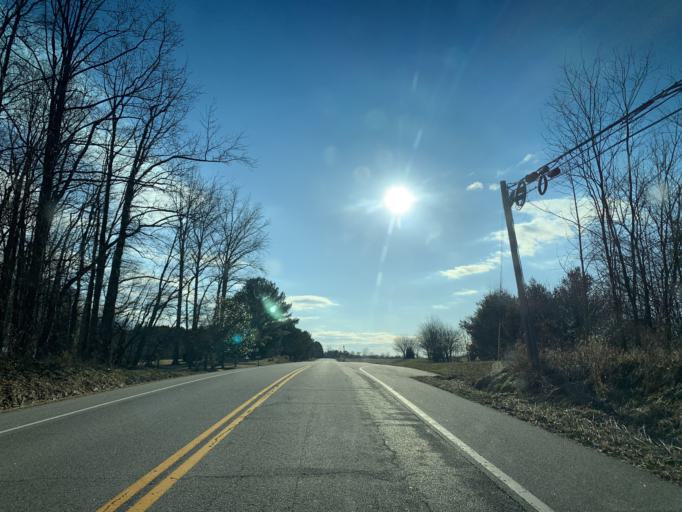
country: US
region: Maryland
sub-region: Queen Anne's County
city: Kingstown
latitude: 39.1517
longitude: -75.9643
